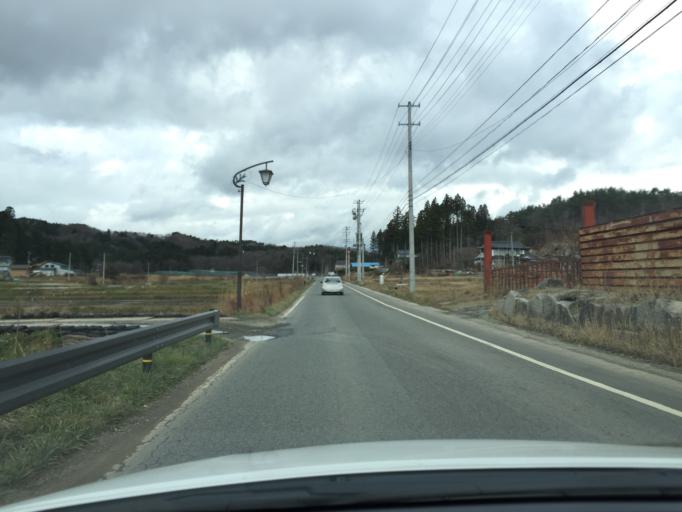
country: JP
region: Fukushima
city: Yanagawamachi-saiwaicho
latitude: 37.7035
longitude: 140.6965
